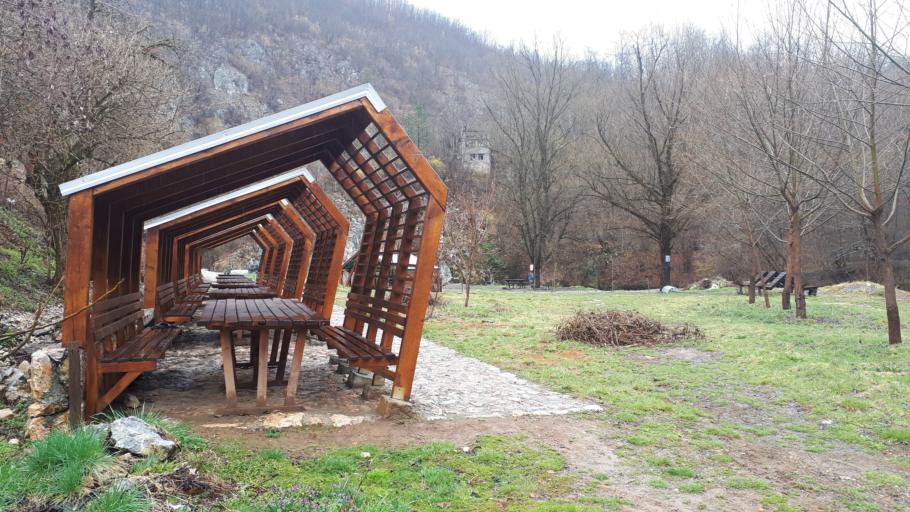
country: RS
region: Central Serbia
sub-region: Zlatiborski Okrug
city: Uzice
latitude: 43.8447
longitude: 19.7653
